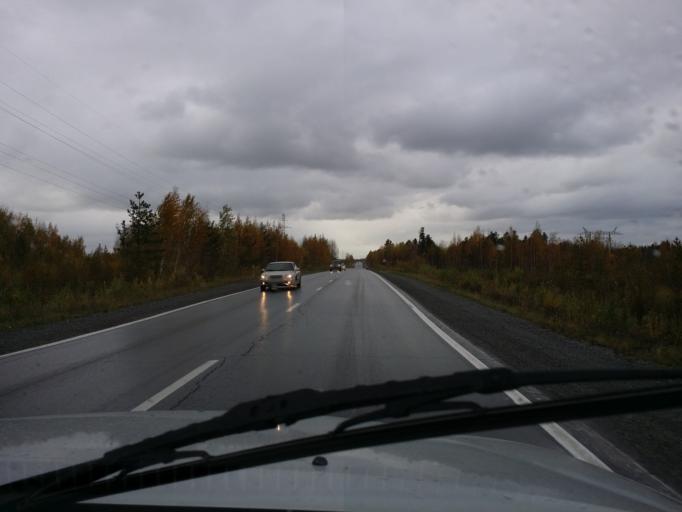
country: RU
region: Khanty-Mansiyskiy Avtonomnyy Okrug
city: Megion
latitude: 61.1046
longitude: 75.9355
